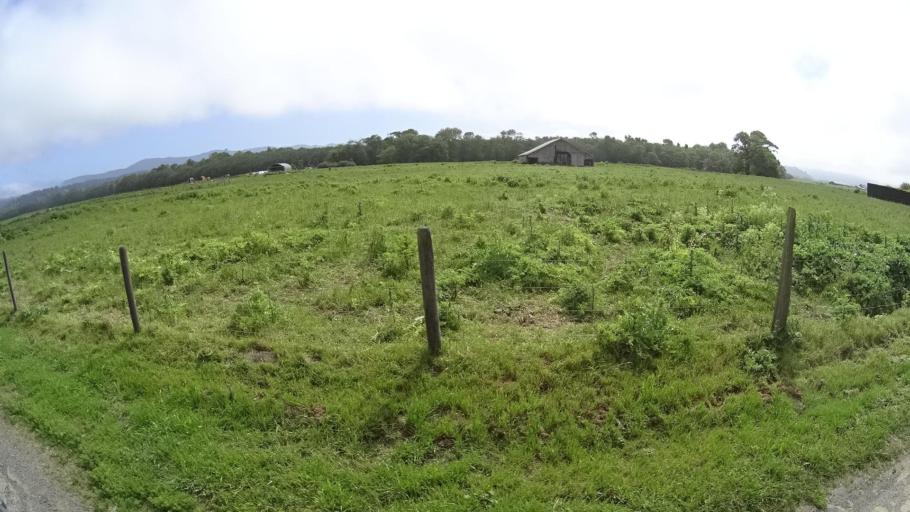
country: US
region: California
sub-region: Humboldt County
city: Fortuna
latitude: 40.5840
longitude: -124.1878
